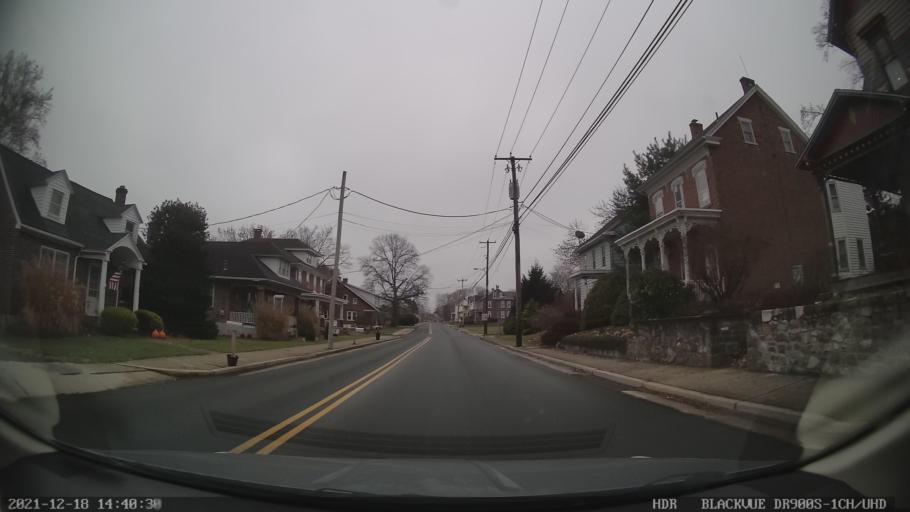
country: US
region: Pennsylvania
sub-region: Berks County
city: New Berlinville
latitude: 40.3694
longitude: -75.6296
